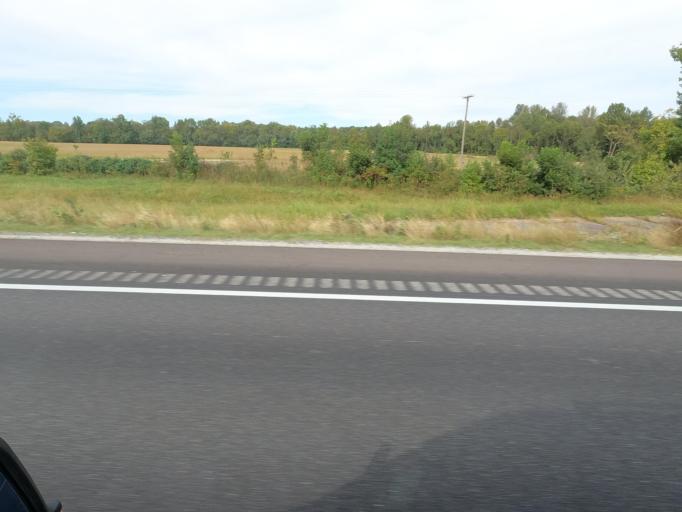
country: US
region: Tennessee
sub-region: Crockett County
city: Bells
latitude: 35.6104
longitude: -89.0210
